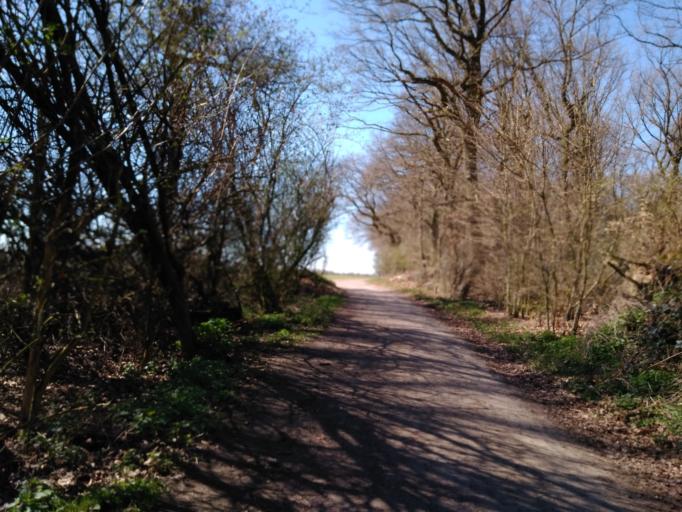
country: DE
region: North Rhine-Westphalia
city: Marl
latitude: 51.6163
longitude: 7.0959
